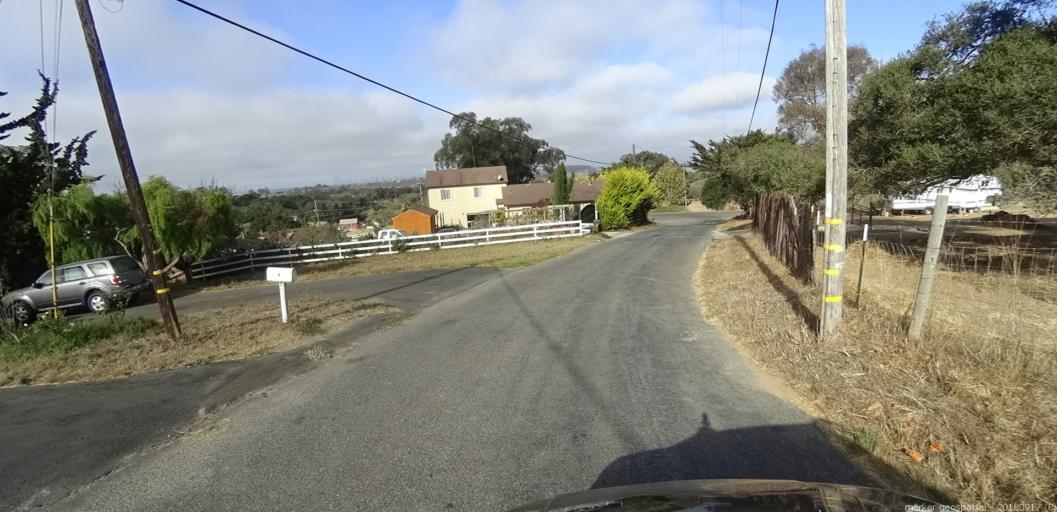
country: US
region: California
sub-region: Monterey County
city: Elkhorn
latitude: 36.8068
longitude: -121.7216
